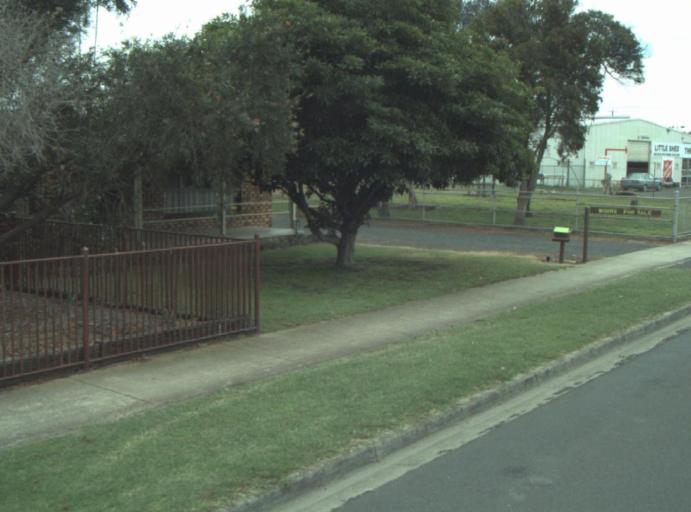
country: AU
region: Victoria
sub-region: Greater Geelong
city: Breakwater
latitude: -38.1749
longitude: 144.4022
